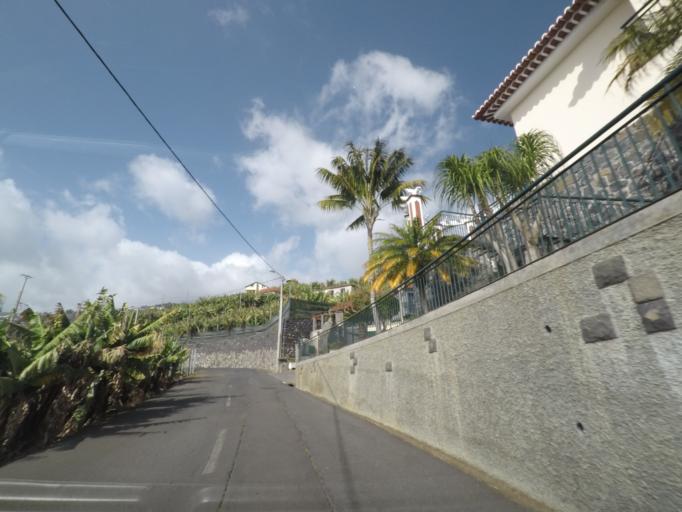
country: PT
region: Madeira
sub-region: Ribeira Brava
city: Campanario
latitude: 32.6729
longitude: -17.0586
